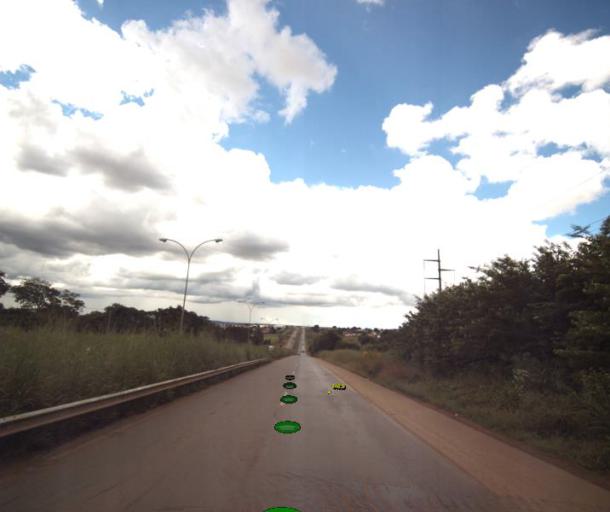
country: BR
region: Goias
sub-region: Anapolis
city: Anapolis
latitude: -16.3511
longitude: -48.9280
